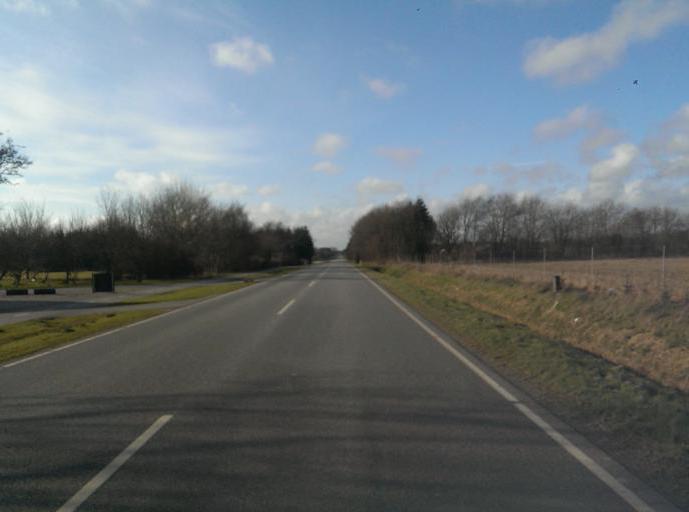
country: DK
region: South Denmark
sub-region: Esbjerg Kommune
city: Bramming
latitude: 55.4521
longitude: 8.7223
